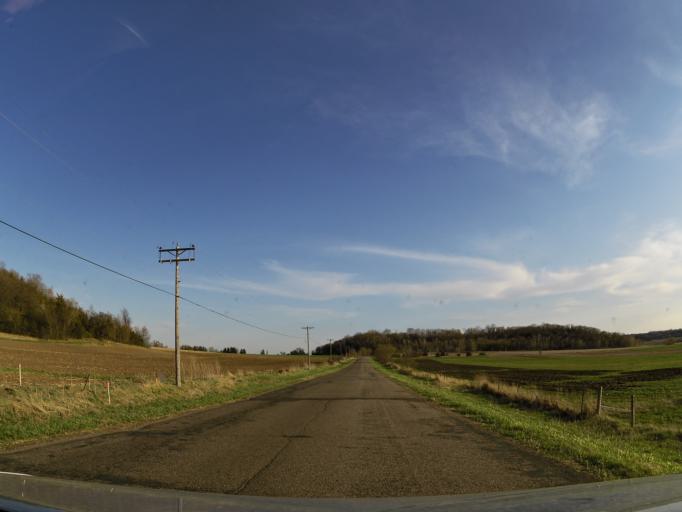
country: US
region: Wisconsin
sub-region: Pierce County
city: River Falls
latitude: 44.8817
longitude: -92.6497
